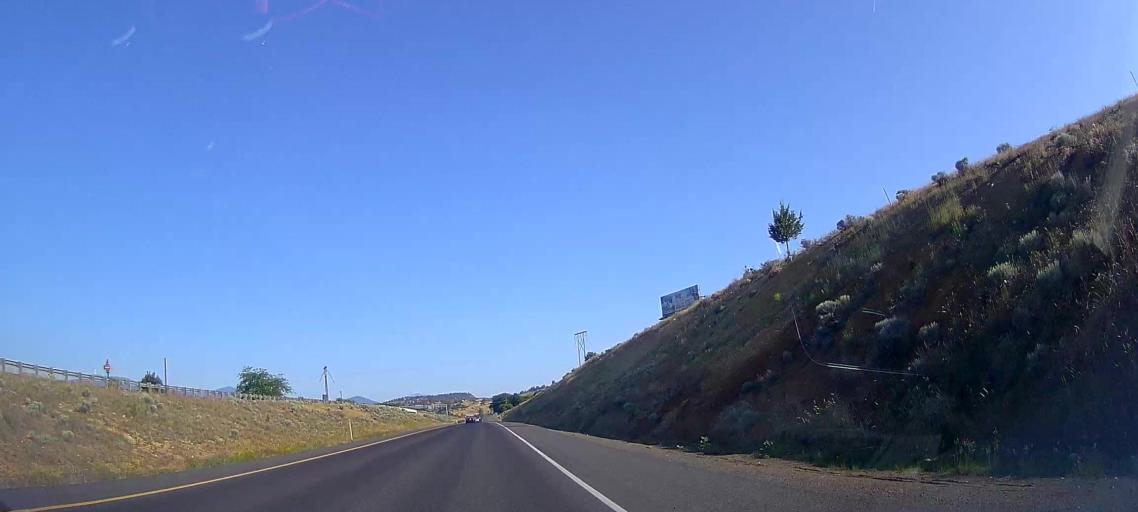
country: US
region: Oregon
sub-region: Klamath County
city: Klamath Falls
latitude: 42.2500
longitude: -121.7925
